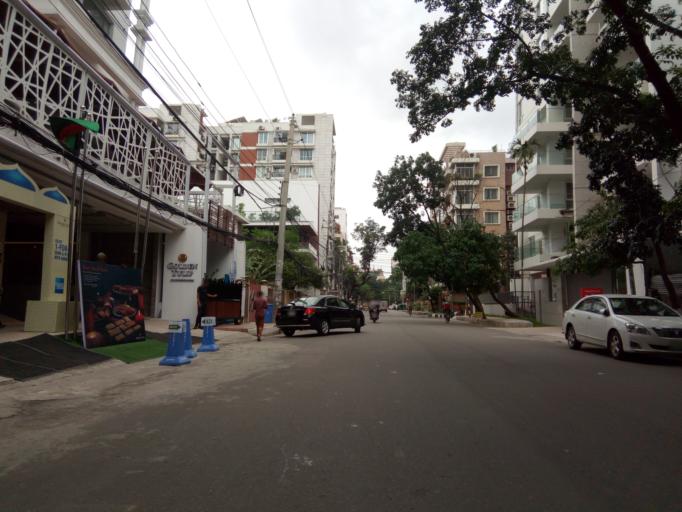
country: BD
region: Dhaka
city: Paltan
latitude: 23.7891
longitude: 90.4072
